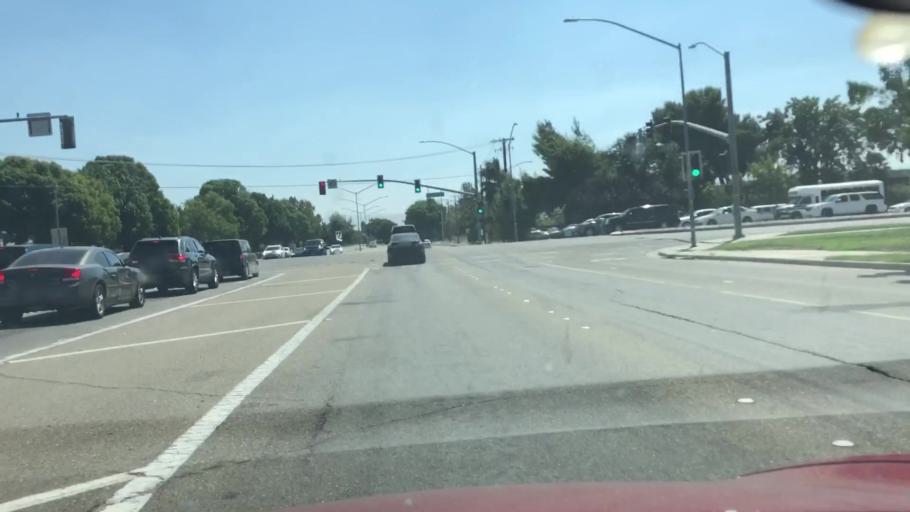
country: US
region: California
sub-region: San Joaquin County
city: Tracy
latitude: 37.7398
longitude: -121.4532
